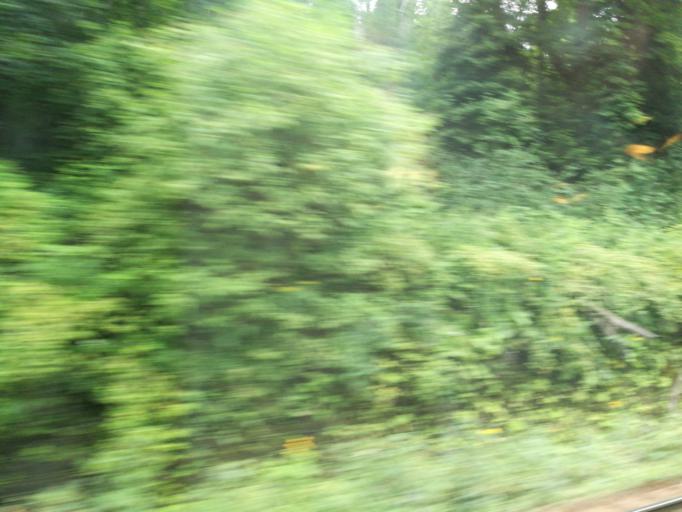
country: RO
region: Brasov
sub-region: Oras Predeal
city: Predeal
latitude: 45.5146
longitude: 25.5837
